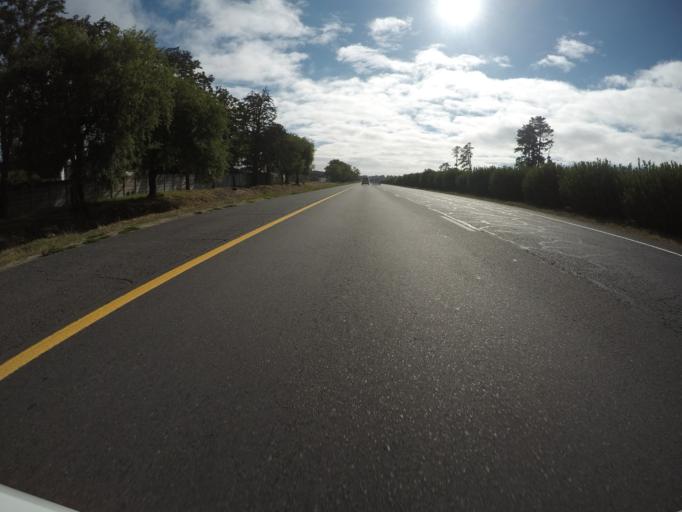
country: ZA
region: Western Cape
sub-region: City of Cape Town
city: Kraaifontein
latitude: -33.8516
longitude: 18.7051
